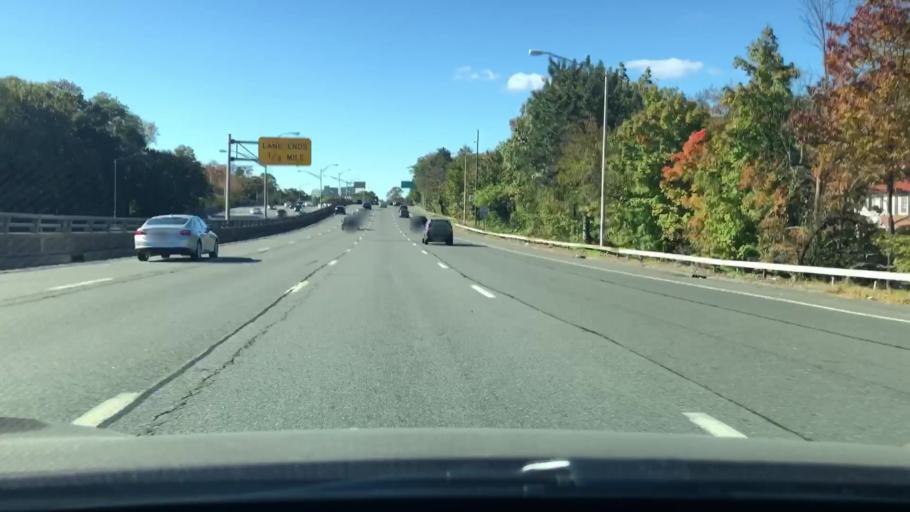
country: US
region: New York
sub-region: Westchester County
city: Pelham
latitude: 40.9225
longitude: -73.8194
